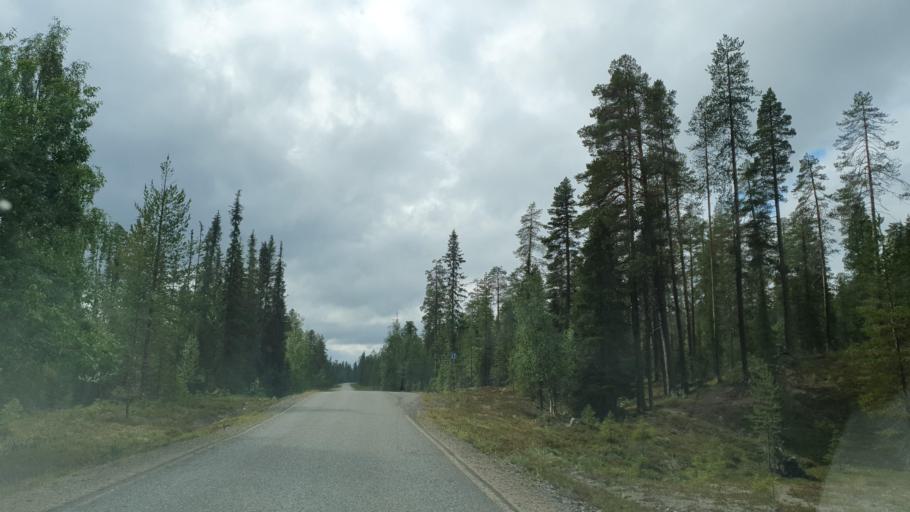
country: FI
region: Lapland
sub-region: Tunturi-Lappi
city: Muonio
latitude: 67.7094
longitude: 24.2023
